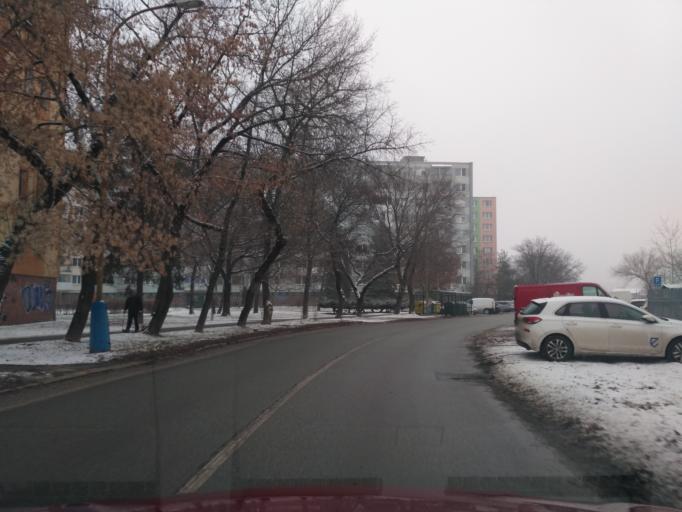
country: SK
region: Kosicky
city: Kosice
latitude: 48.7057
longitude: 21.2350
